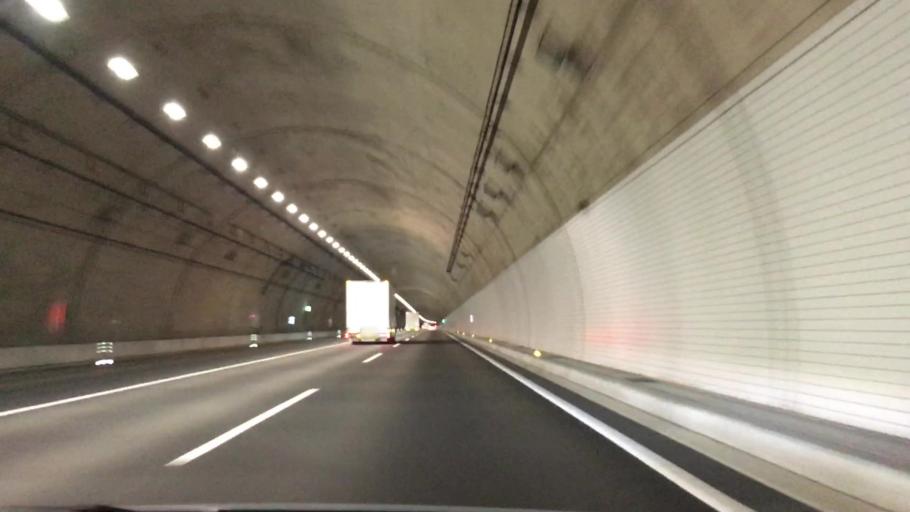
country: JP
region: Shizuoka
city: Hamakita
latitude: 34.8529
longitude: 137.7093
